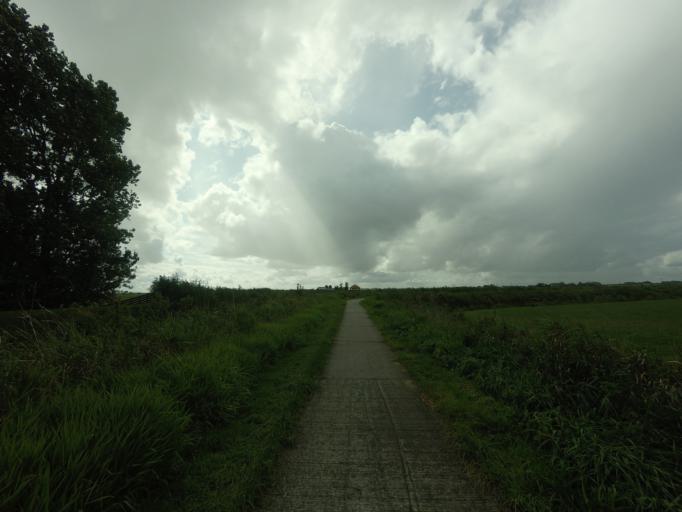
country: NL
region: Friesland
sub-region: Gemeente Leeuwarden
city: Wirdum
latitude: 53.1434
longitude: 5.8241
